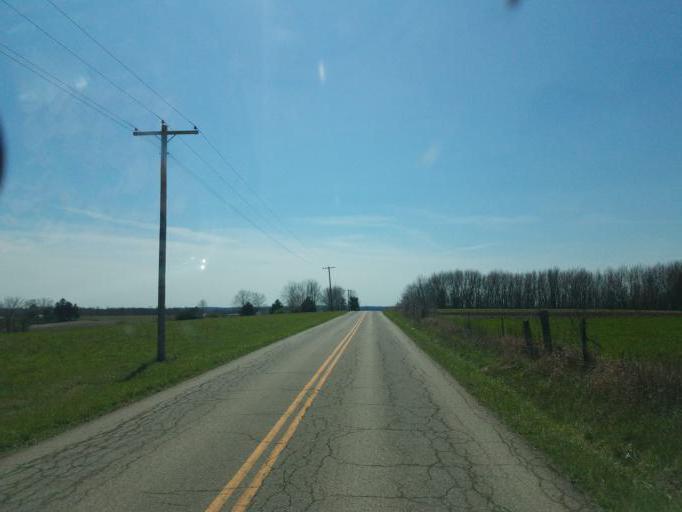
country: US
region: Ohio
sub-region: Knox County
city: Oak Hill
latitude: 40.3140
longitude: -82.2782
